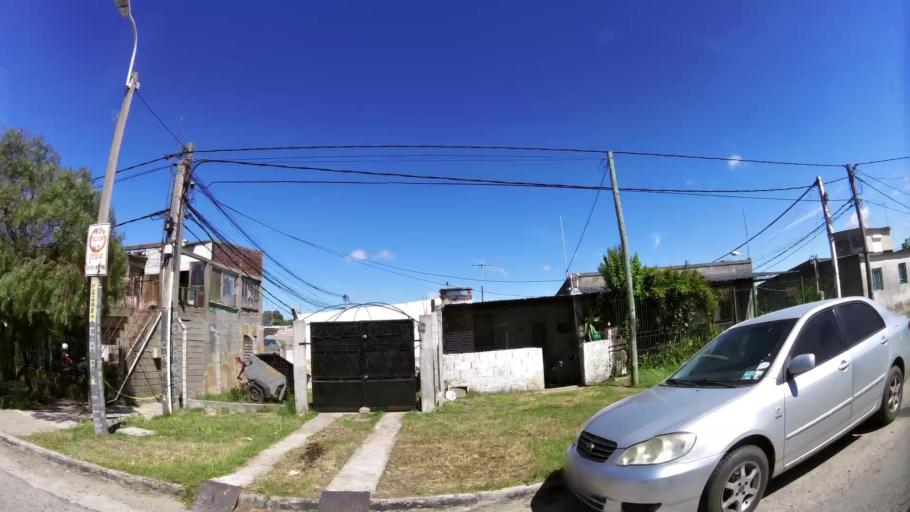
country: UY
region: Canelones
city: Paso de Carrasco
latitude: -34.8470
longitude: -56.1139
